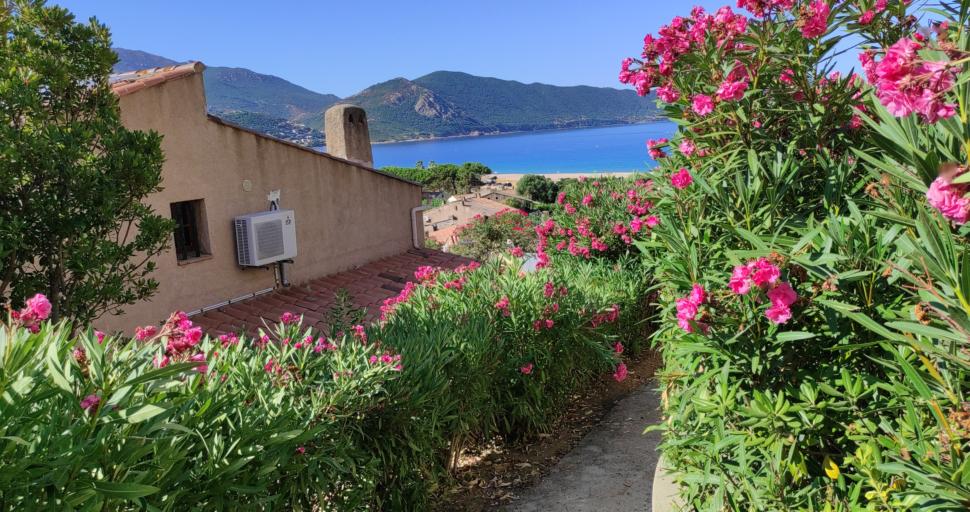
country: FR
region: Corsica
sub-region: Departement de la Corse-du-Sud
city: Alata
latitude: 41.9931
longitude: 8.6717
